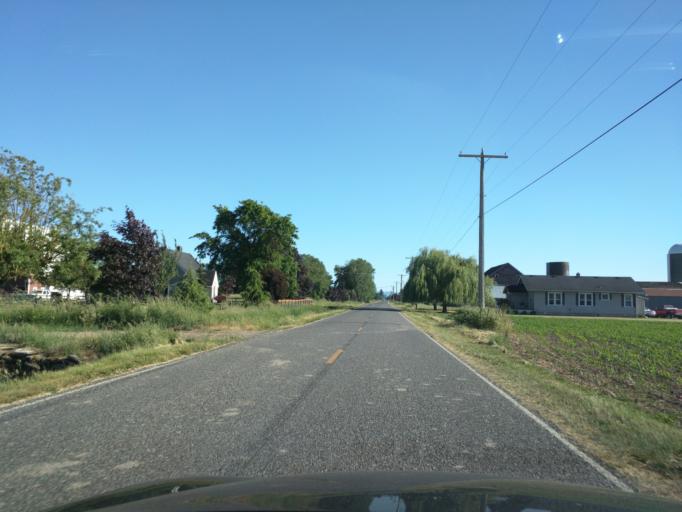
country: US
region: Washington
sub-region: Whatcom County
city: Lynden
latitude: 48.9744
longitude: -122.4408
